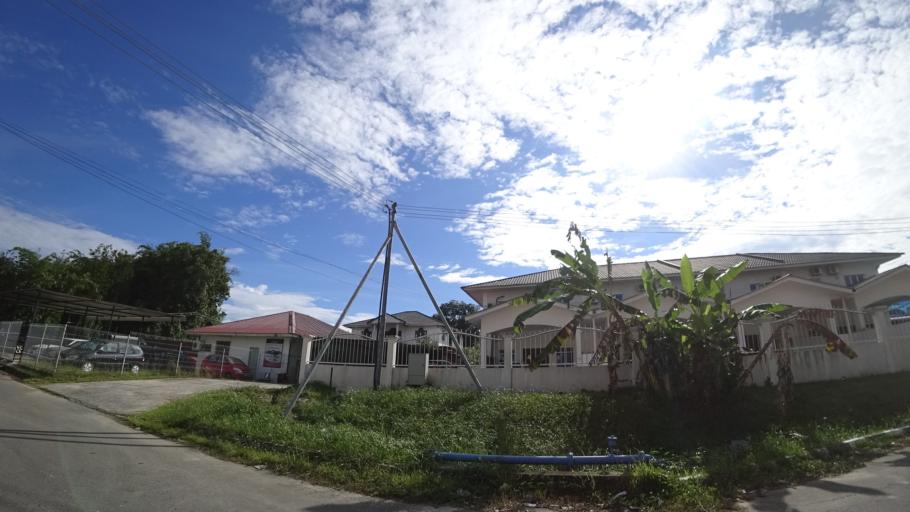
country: BN
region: Brunei and Muara
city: Bandar Seri Begawan
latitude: 4.8878
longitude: 114.8569
